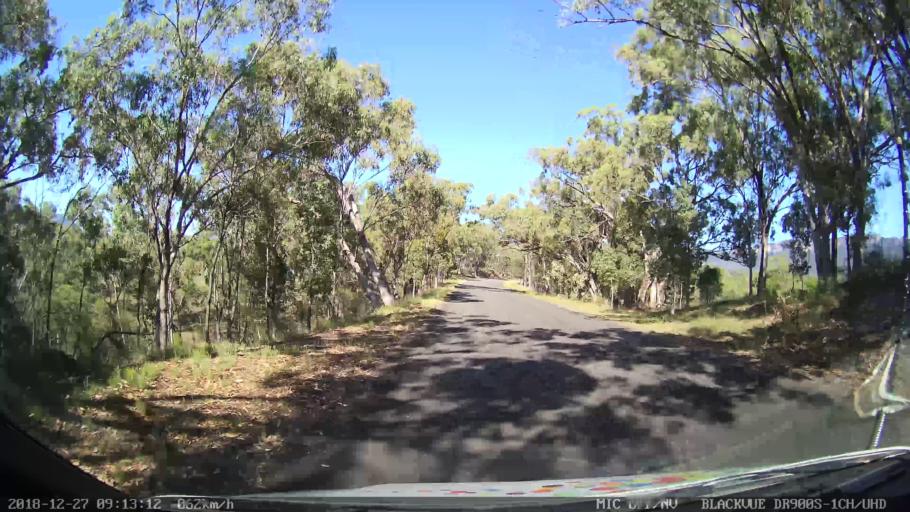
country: AU
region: New South Wales
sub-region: Lithgow
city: Portland
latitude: -33.1379
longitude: 150.0966
